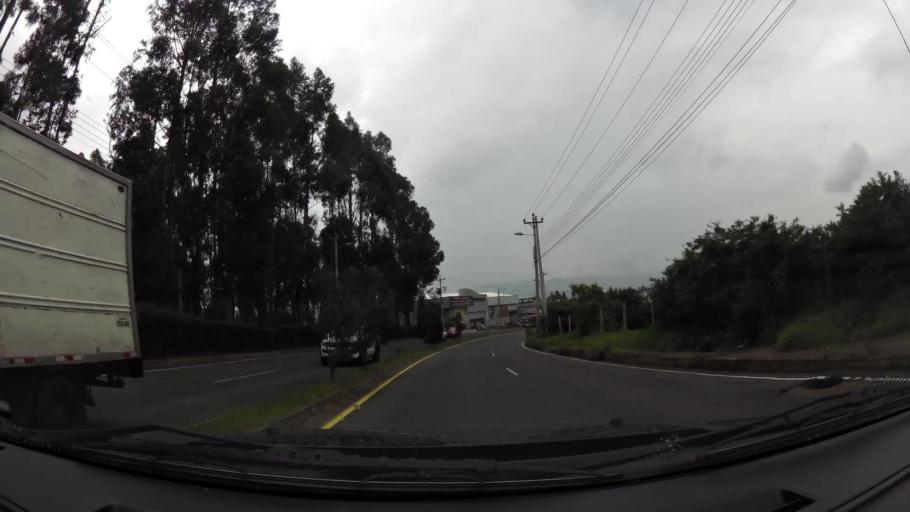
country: EC
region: Pichincha
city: Sangolqui
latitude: -0.3273
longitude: -78.4389
